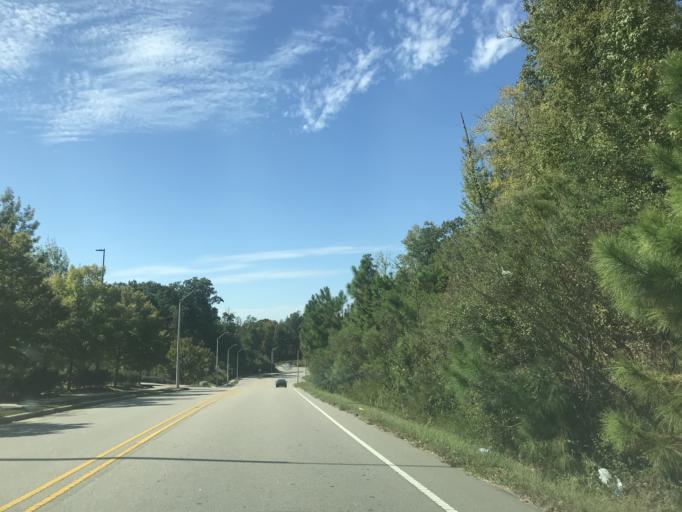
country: US
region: North Carolina
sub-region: Wake County
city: Knightdale
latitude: 35.8708
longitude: -78.5670
